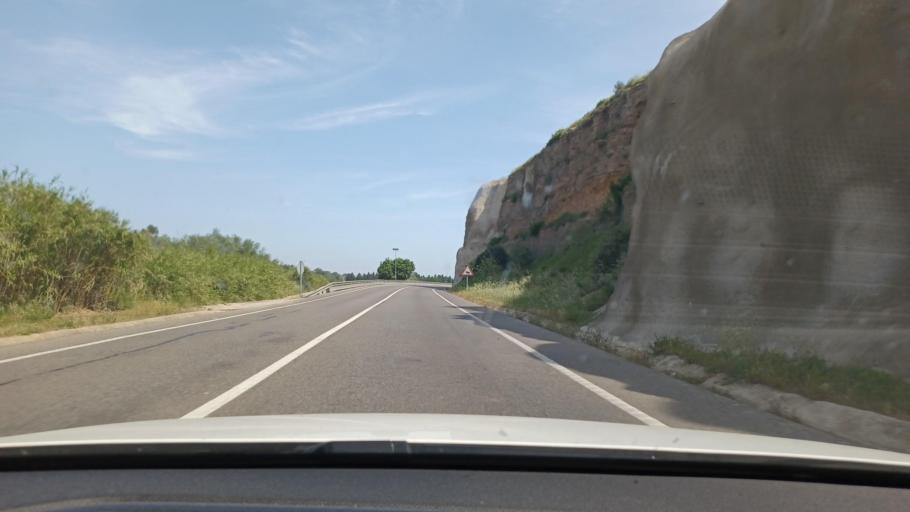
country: ES
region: Catalonia
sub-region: Provincia de Tarragona
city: Tortosa
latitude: 40.7862
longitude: 0.4999
